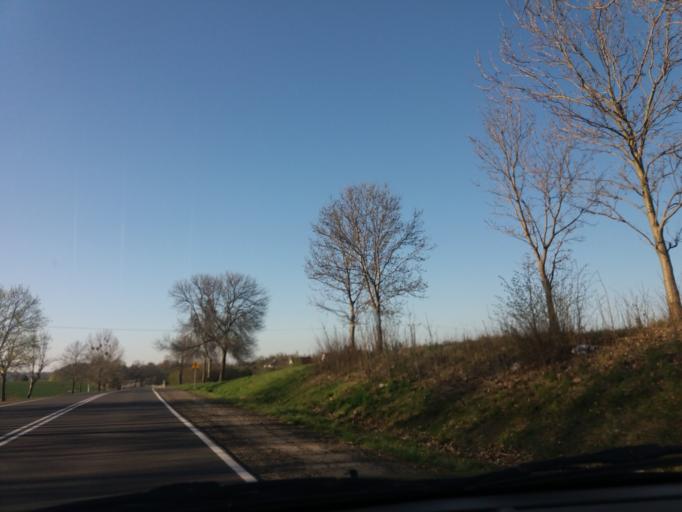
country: PL
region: Warmian-Masurian Voivodeship
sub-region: Powiat nidzicki
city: Nidzica
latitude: 53.3424
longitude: 20.4342
